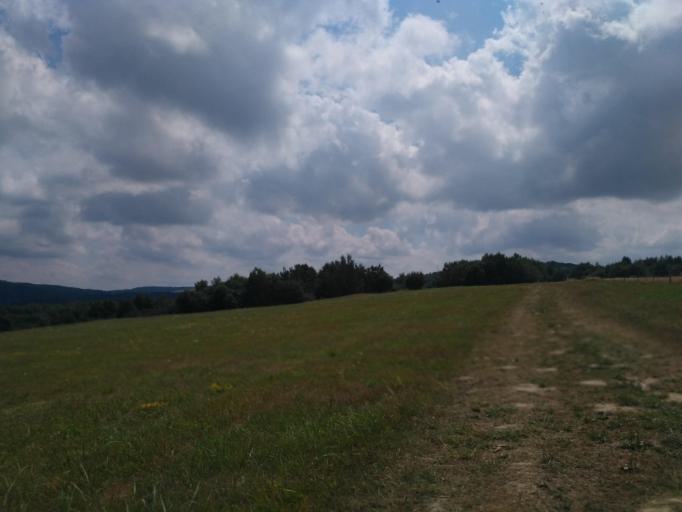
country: PL
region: Subcarpathian Voivodeship
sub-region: Powiat krosnienski
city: Iwonicz-Zdroj
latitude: 49.5770
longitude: 21.7777
